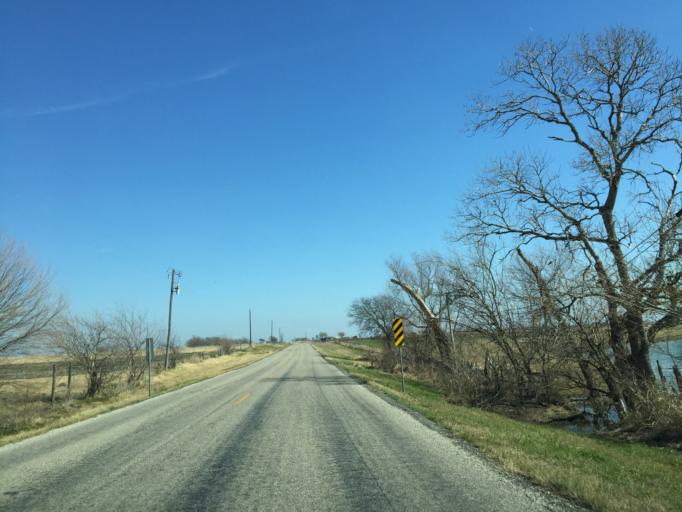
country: US
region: Texas
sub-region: Williamson County
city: Granger
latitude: 30.7513
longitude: -97.5516
